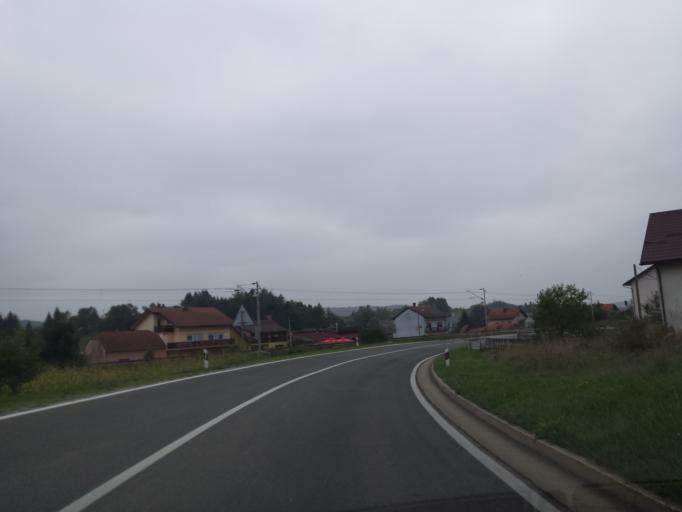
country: HR
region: Karlovacka
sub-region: Grad Karlovac
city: Karlovac
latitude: 45.4375
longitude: 15.4969
